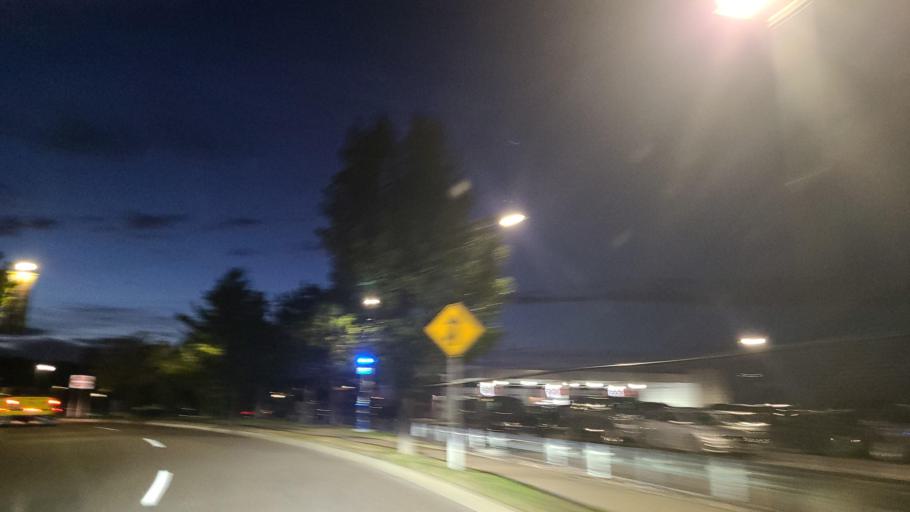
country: US
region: Vermont
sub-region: Chittenden County
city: South Burlington
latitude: 44.4714
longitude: -73.1563
